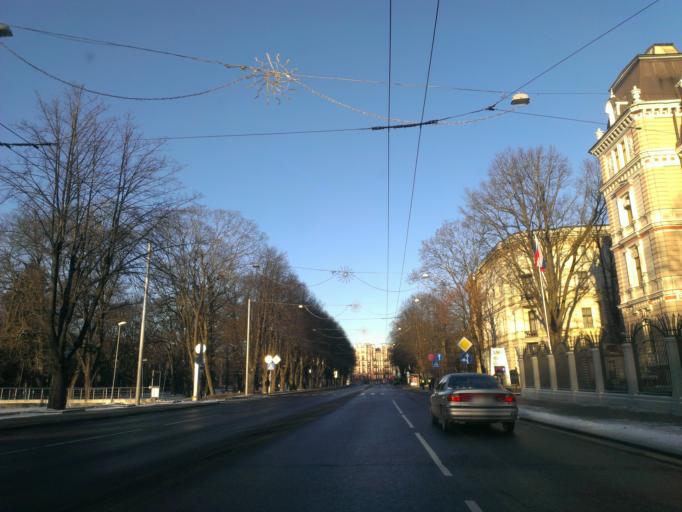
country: LV
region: Riga
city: Riga
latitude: 56.9561
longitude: 24.1086
